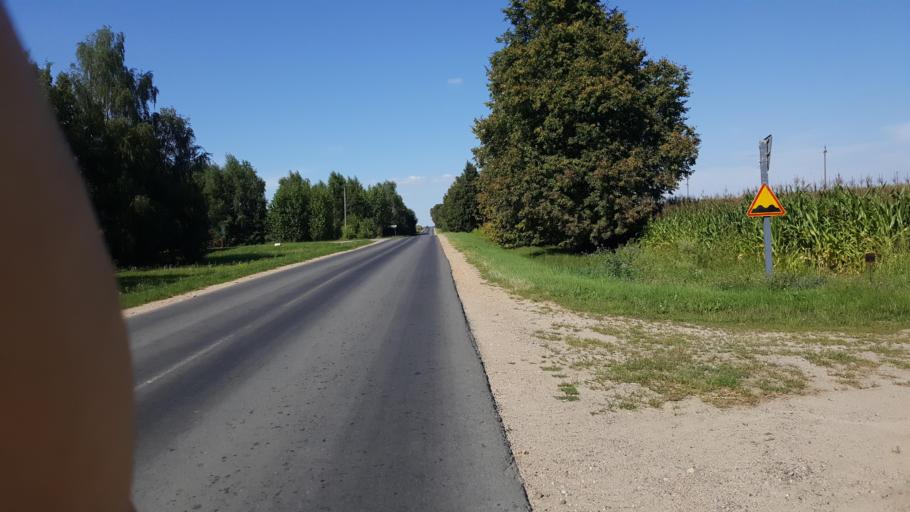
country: BY
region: Brest
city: Charnawchytsy
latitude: 52.2821
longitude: 23.6033
